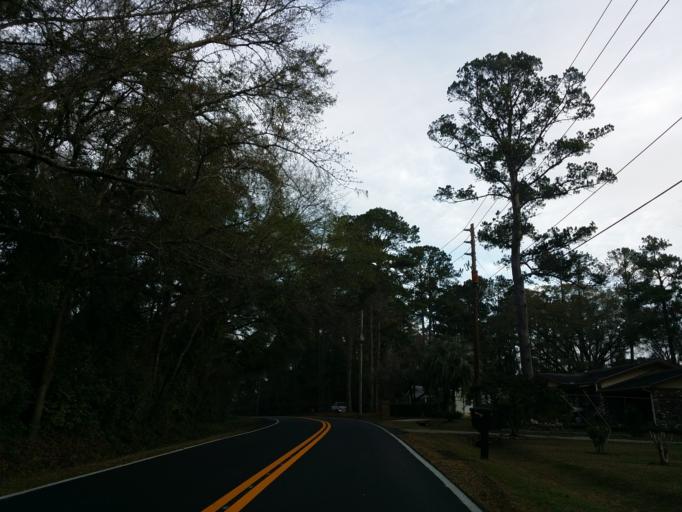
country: US
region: Florida
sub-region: Leon County
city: Tallahassee
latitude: 30.4699
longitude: -84.2148
